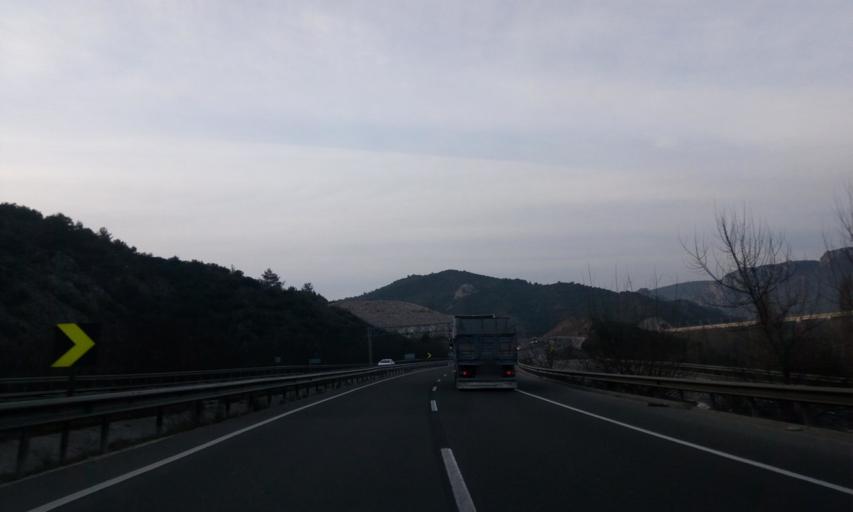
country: TR
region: Bilecik
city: Bilecik
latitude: 40.1623
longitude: 30.0211
